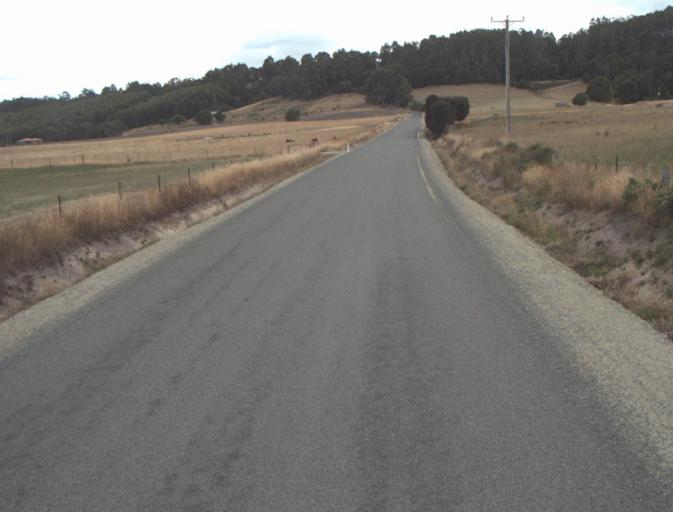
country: AU
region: Tasmania
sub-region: Launceston
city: Mayfield
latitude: -41.2060
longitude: 147.1883
